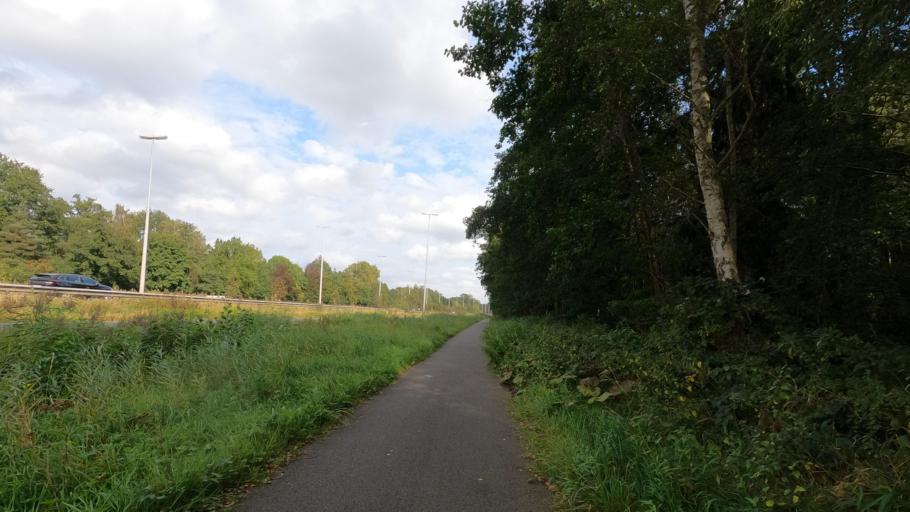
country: BE
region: Flanders
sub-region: Provincie Oost-Vlaanderen
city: Stekene
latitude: 51.2279
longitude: 4.0678
